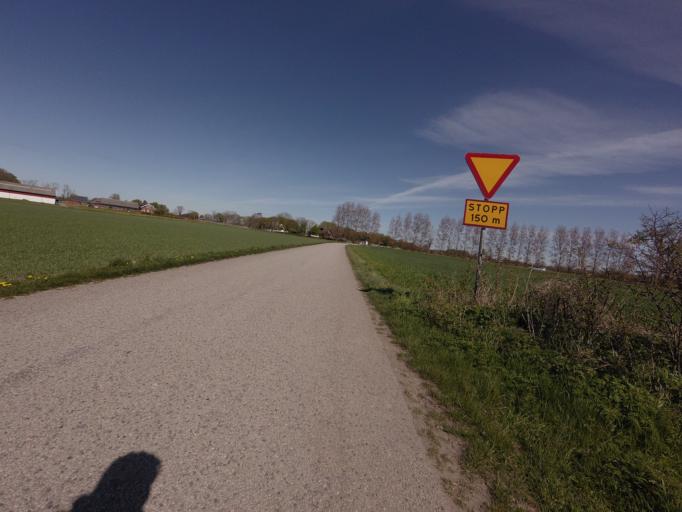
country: SE
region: Skane
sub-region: Hoganas Kommun
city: Hoganas
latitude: 56.1798
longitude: 12.5908
